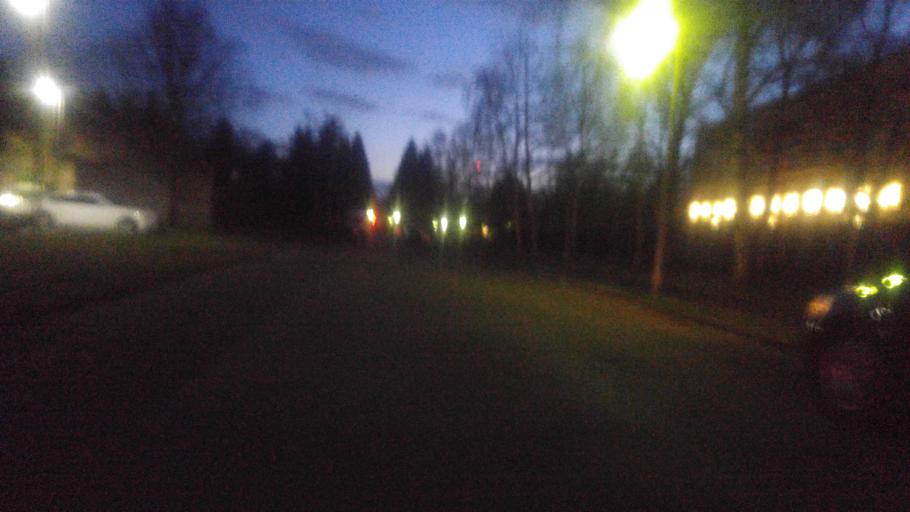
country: DE
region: Berlin
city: Haselhorst
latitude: 52.5266
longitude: 13.2314
